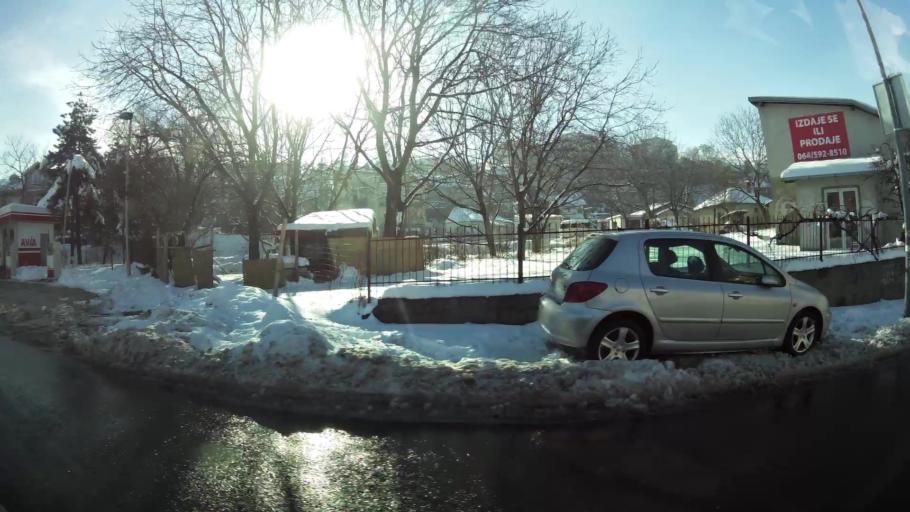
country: RS
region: Central Serbia
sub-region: Belgrade
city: Palilula
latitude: 44.8156
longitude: 20.5049
